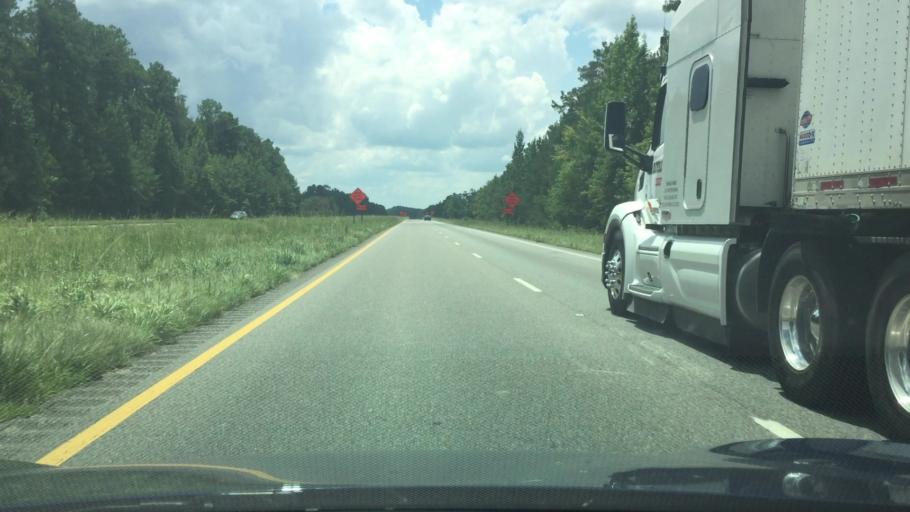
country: US
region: Alabama
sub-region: Pike County
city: Troy
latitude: 31.9877
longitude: -86.0269
